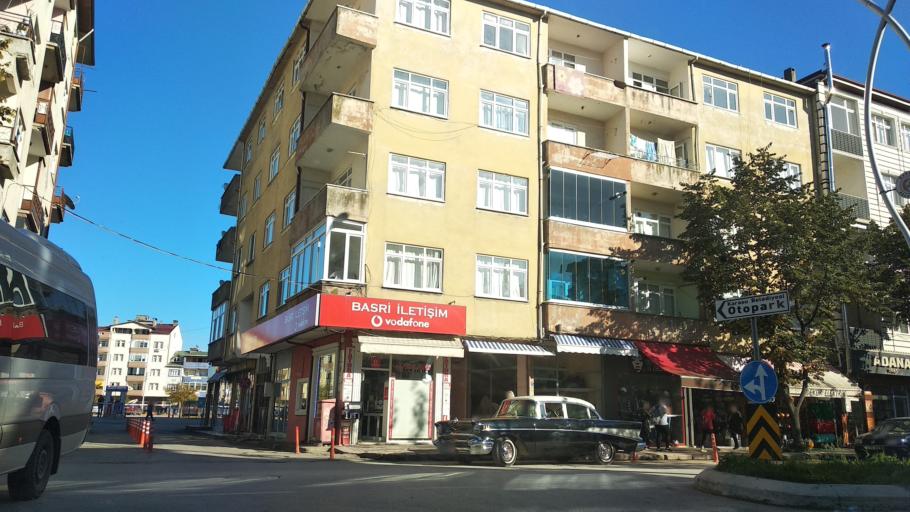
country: TR
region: Sakarya
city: Karasu
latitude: 41.0966
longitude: 30.6924
